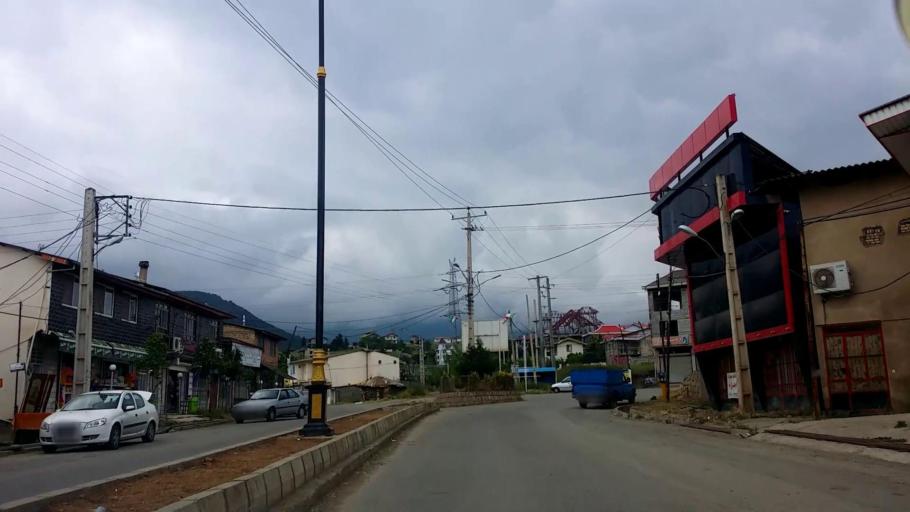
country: IR
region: Mazandaran
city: Chalus
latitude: 36.5112
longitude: 51.2471
